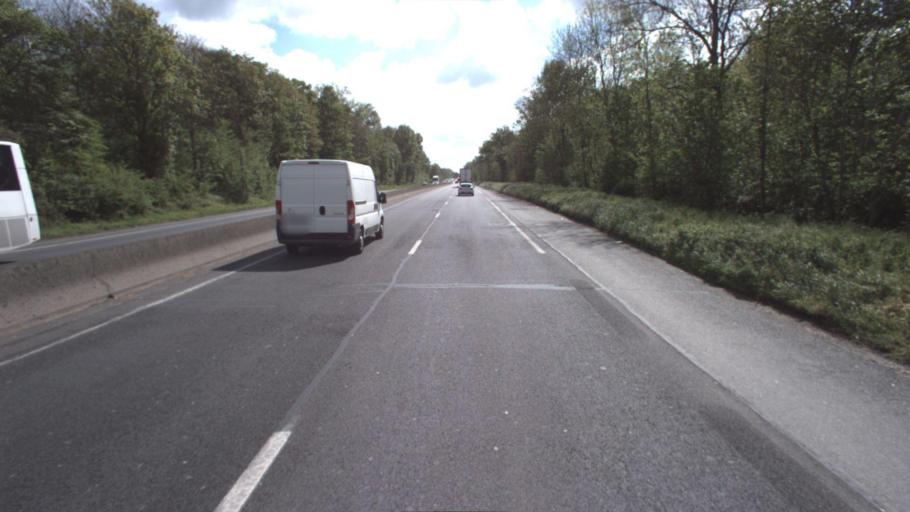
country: FR
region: Ile-de-France
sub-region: Departement de Seine-et-Marne
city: Roissy-en-Brie
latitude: 48.7710
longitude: 2.6278
